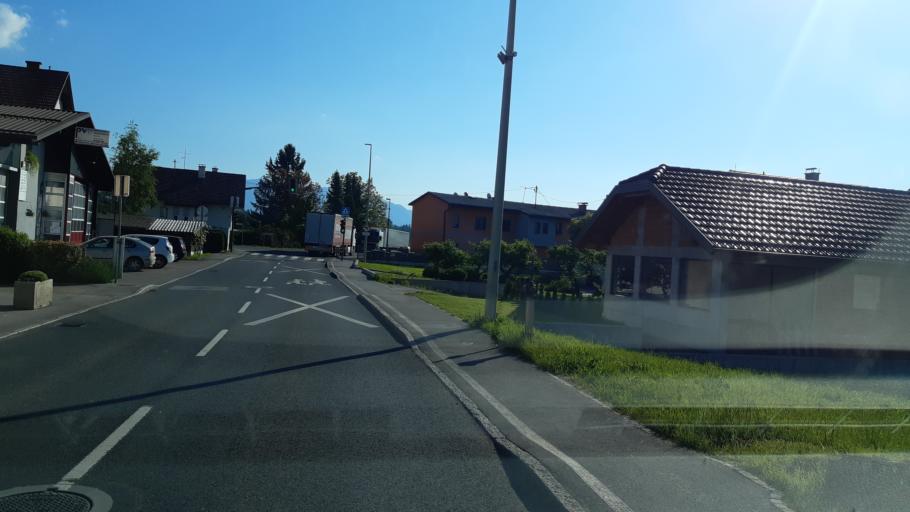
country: SI
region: Vodice
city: Vodice
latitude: 46.1893
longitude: 14.4987
